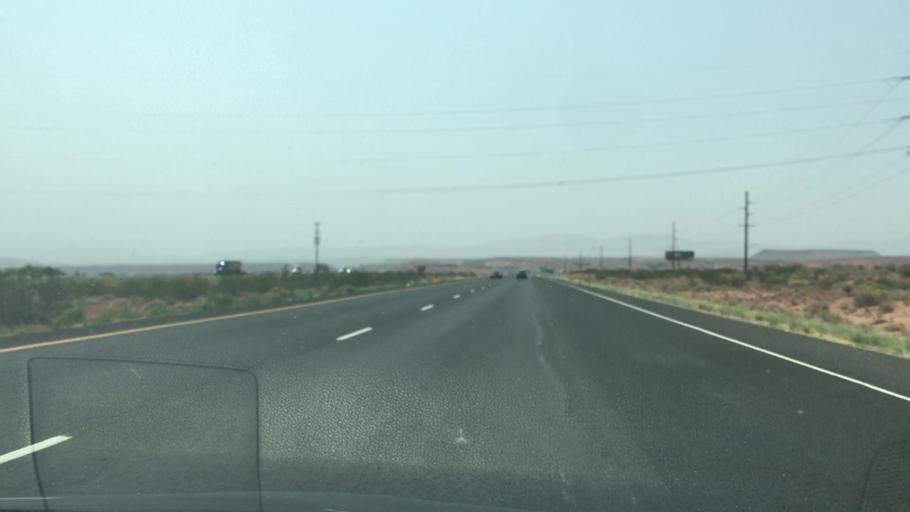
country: US
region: Utah
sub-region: Washington County
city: Washington
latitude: 37.1460
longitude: -113.4921
